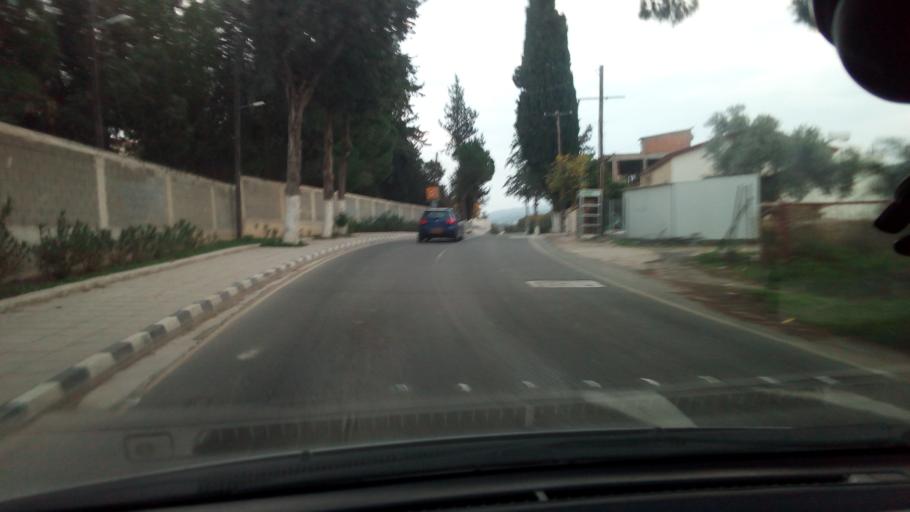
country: CY
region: Pafos
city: Polis
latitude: 35.0317
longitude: 32.4282
